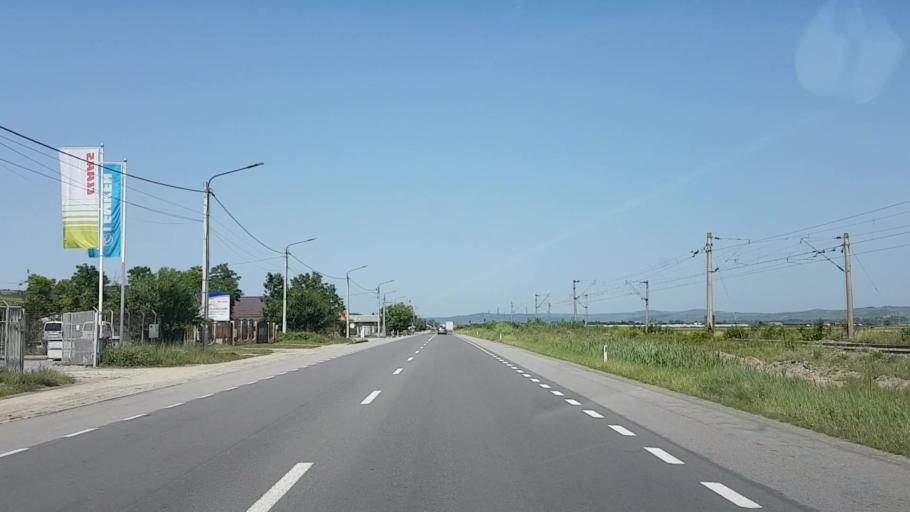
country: RO
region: Cluj
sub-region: Comuna Apahida
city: Apahida
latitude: 46.8406
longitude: 23.7487
